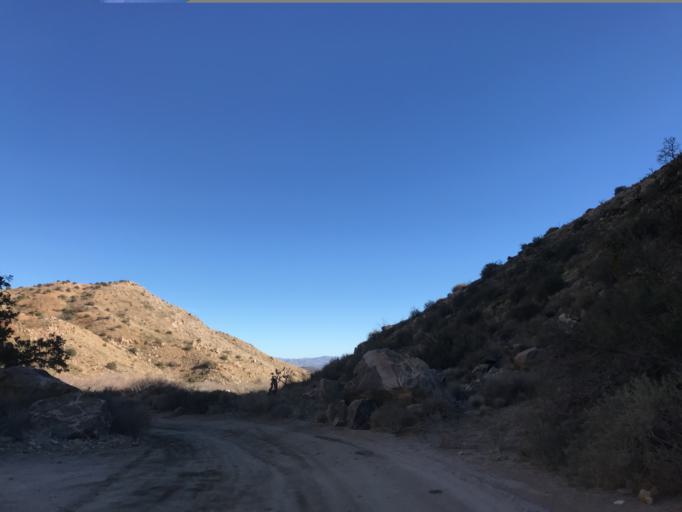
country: US
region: California
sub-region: San Bernardino County
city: Morongo Valley
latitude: 34.2048
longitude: -116.5798
